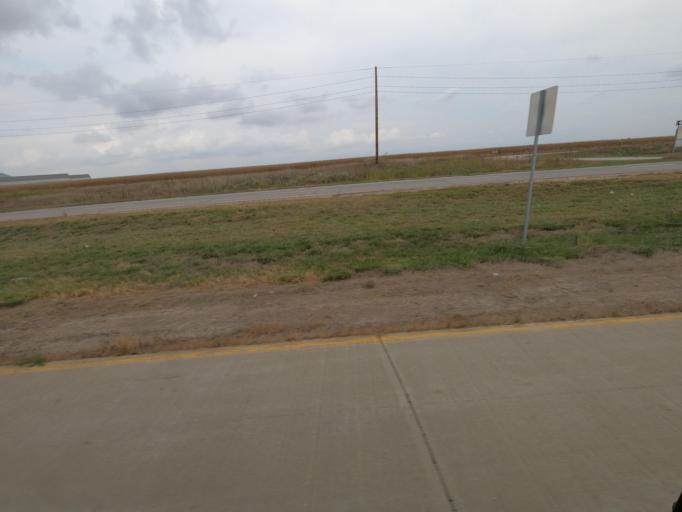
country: US
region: Iowa
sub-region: Jasper County
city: Monroe
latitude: 41.5526
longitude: -93.1388
